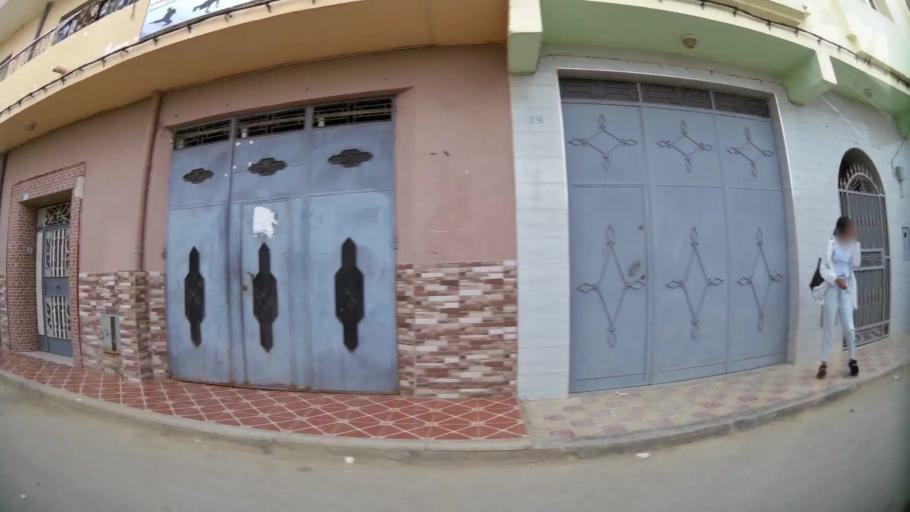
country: MA
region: Oriental
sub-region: Nador
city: Nador
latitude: 35.1675
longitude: -2.9387
